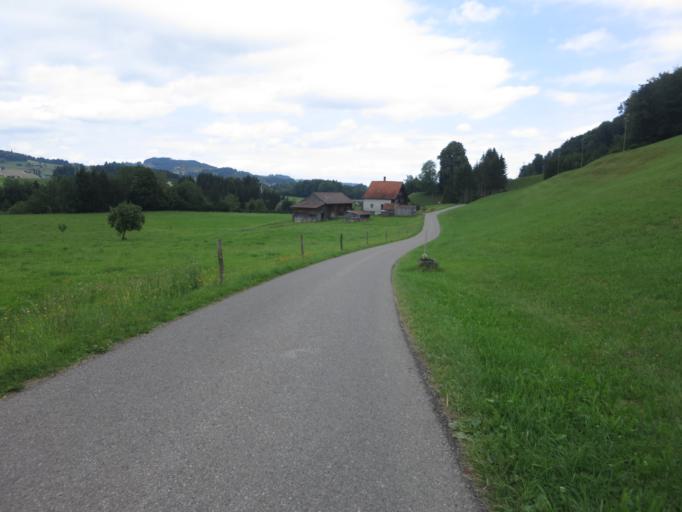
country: CH
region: Saint Gallen
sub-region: Wahlkreis Toggenburg
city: Ganterschwil
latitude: 47.3692
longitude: 9.0839
